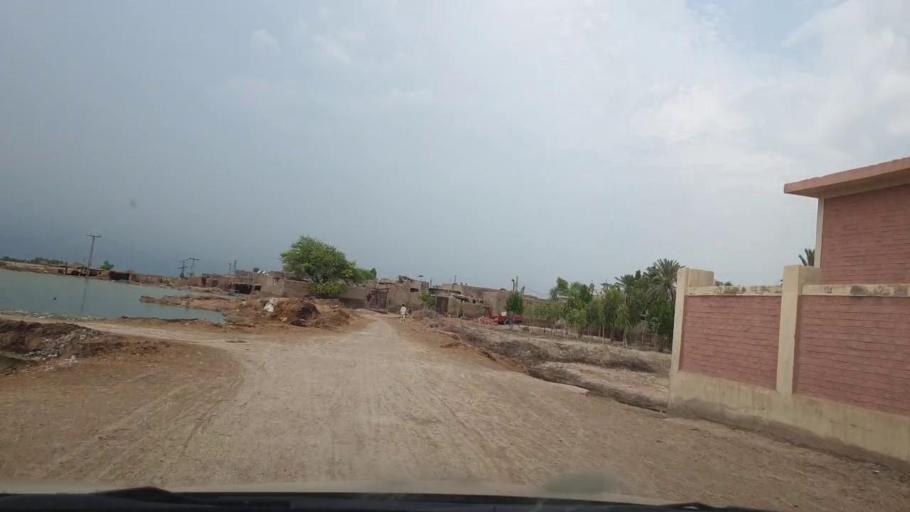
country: PK
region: Sindh
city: Ratodero
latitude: 27.8205
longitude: 68.3174
